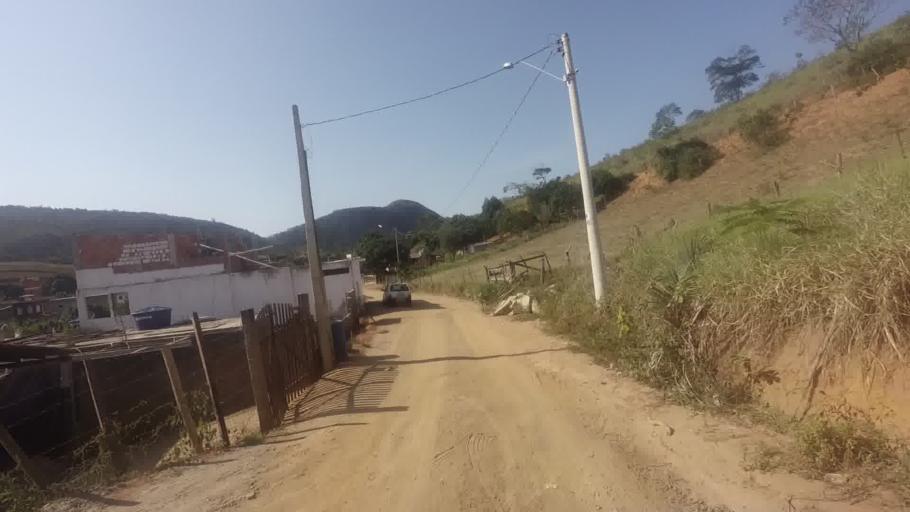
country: BR
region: Espirito Santo
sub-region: Piuma
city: Piuma
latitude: -20.8866
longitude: -40.7752
